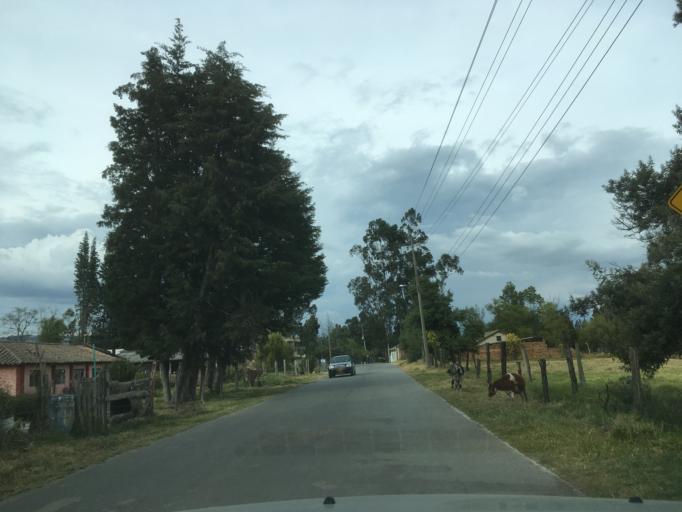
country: CO
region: Boyaca
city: Firavitoba
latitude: 5.6513
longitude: -72.9892
